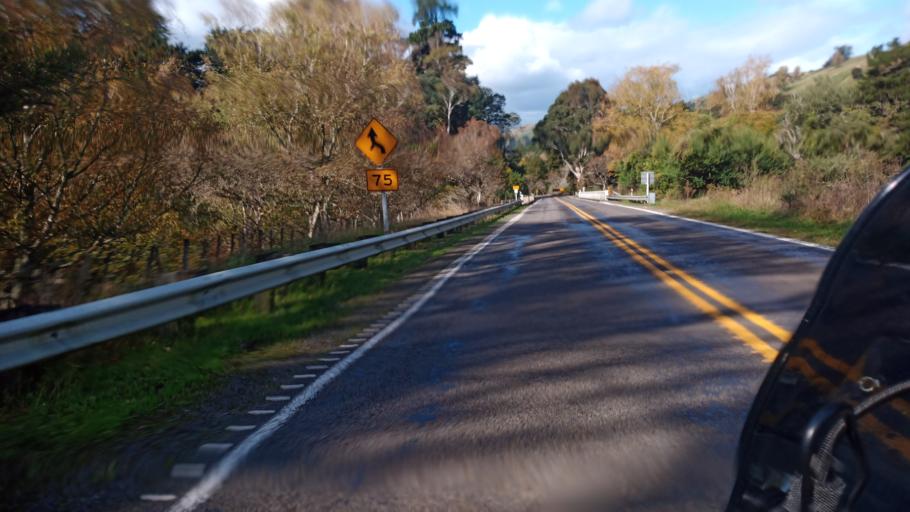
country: NZ
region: Gisborne
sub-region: Gisborne District
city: Gisborne
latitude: -38.4629
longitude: 177.6501
